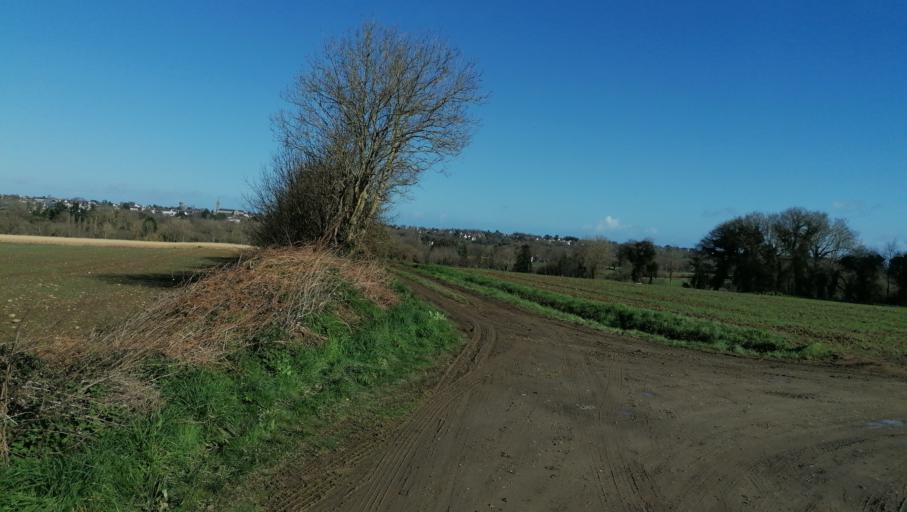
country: FR
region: Brittany
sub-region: Departement des Cotes-d'Armor
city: Plouha
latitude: 48.6599
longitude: -2.9247
